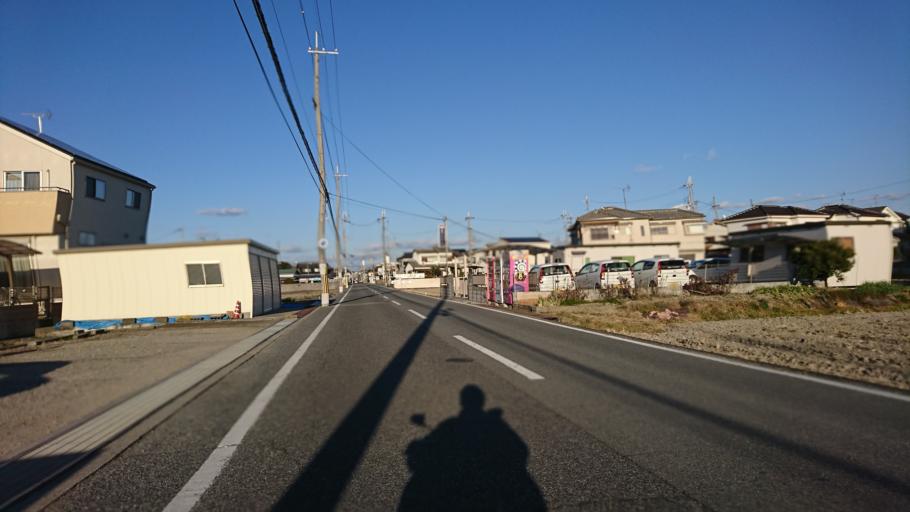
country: JP
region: Hyogo
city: Kakogawacho-honmachi
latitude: 34.7569
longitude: 134.8161
